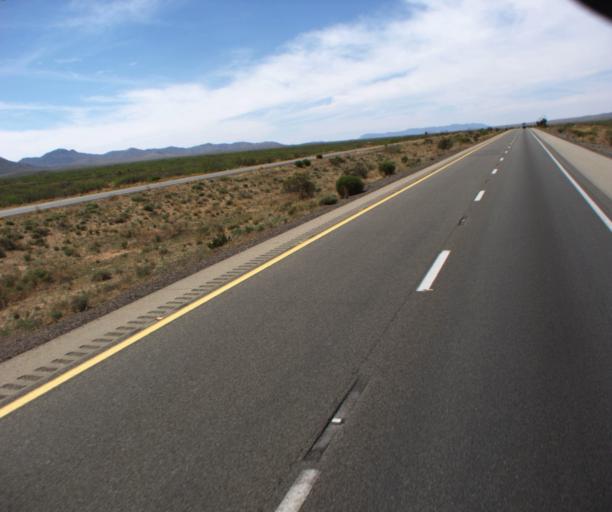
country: US
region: Arizona
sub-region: Cochise County
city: Willcox
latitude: 32.3392
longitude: -109.5549
